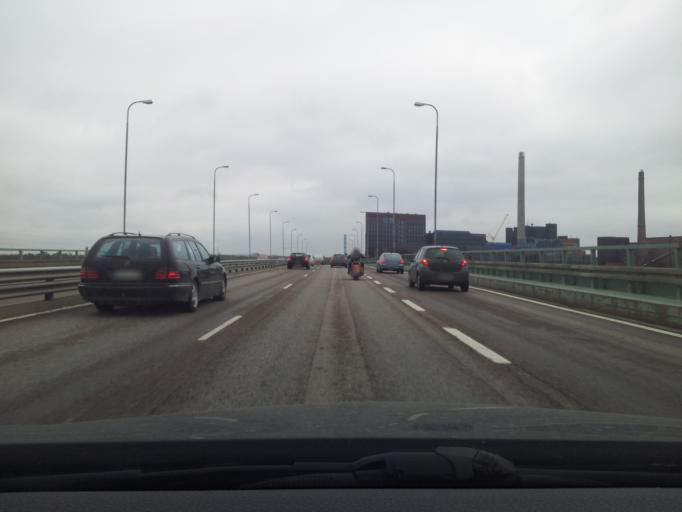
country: FI
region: Uusimaa
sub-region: Helsinki
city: Helsinki
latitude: 60.1659
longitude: 24.8911
